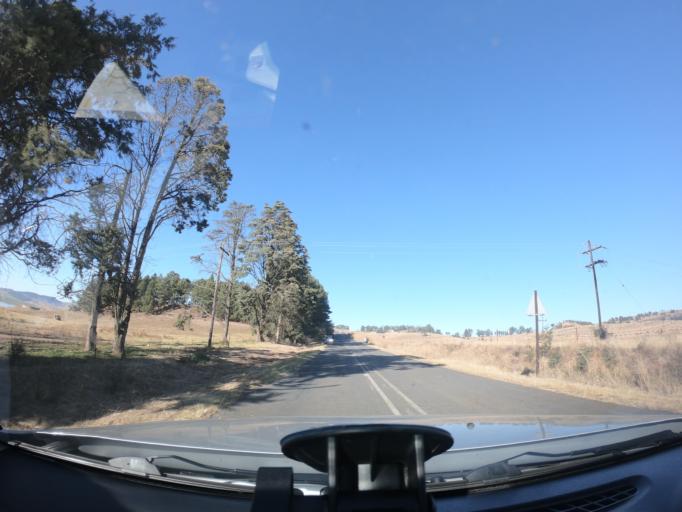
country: ZA
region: KwaZulu-Natal
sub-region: uMgungundlovu District Municipality
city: Mooirivier
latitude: -29.3186
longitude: 29.9211
